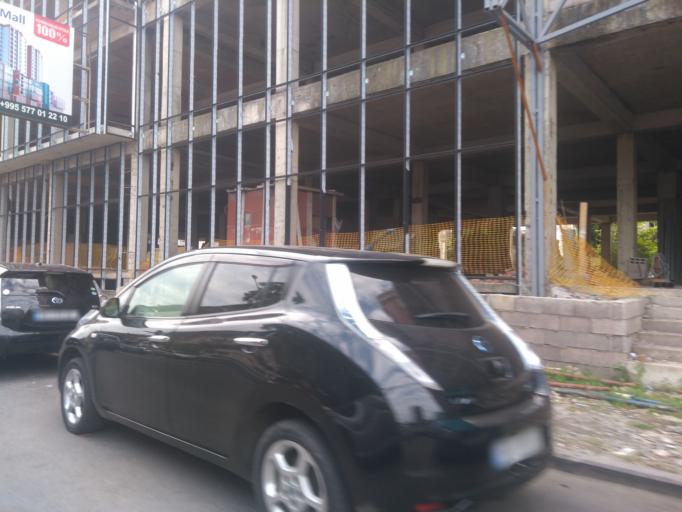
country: GE
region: Ajaria
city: Batumi
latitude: 41.6440
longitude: 41.6428
